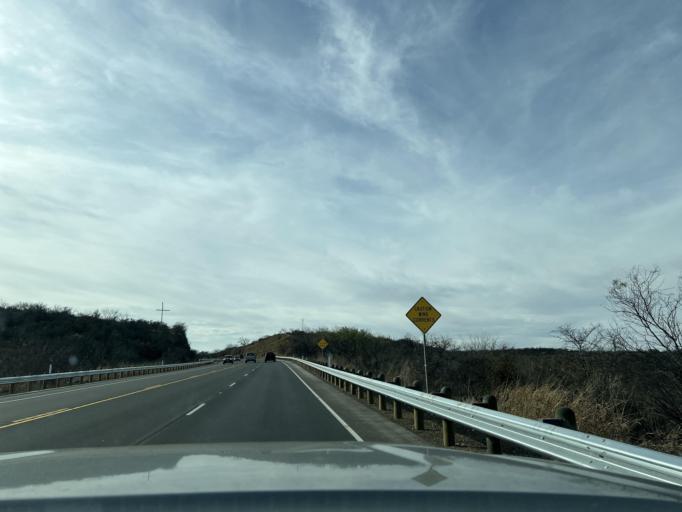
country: US
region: Texas
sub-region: Shackelford County
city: Albany
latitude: 32.7180
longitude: -99.3137
